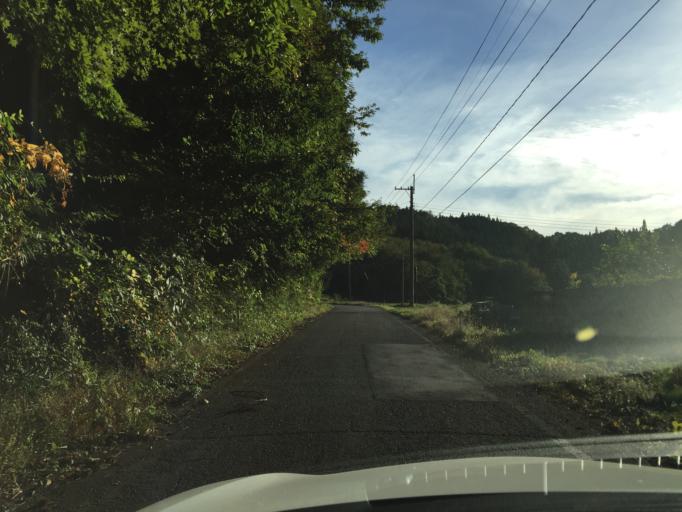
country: JP
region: Fukushima
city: Ishikawa
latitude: 37.2454
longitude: 140.6079
